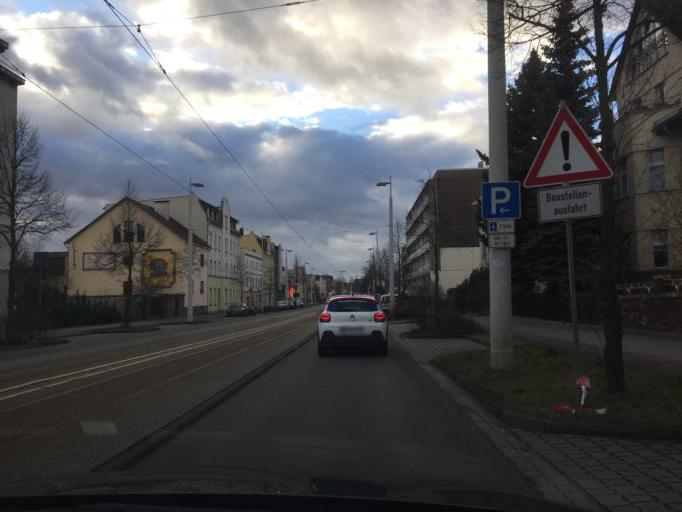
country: DE
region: Brandenburg
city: Cottbus
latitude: 51.7562
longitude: 14.3077
